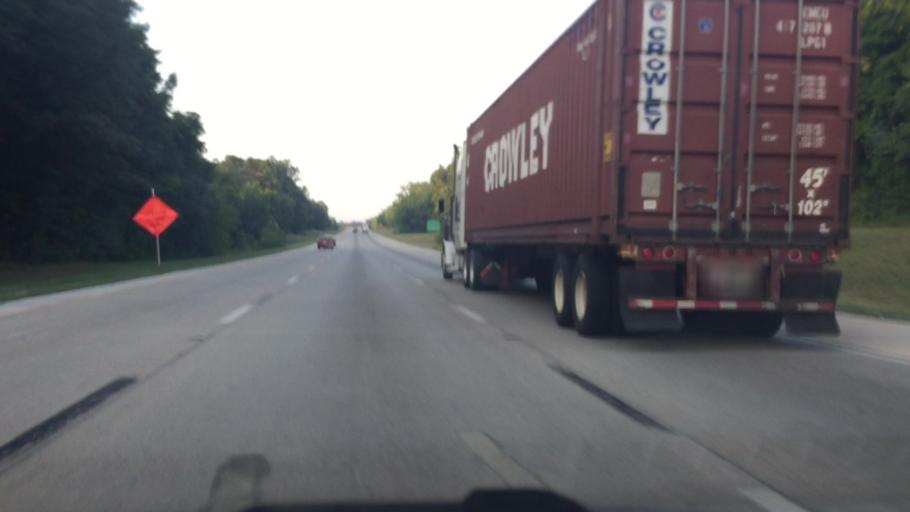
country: US
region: North Carolina
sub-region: Guilford County
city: Jamestown
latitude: 35.9747
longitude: -79.8911
